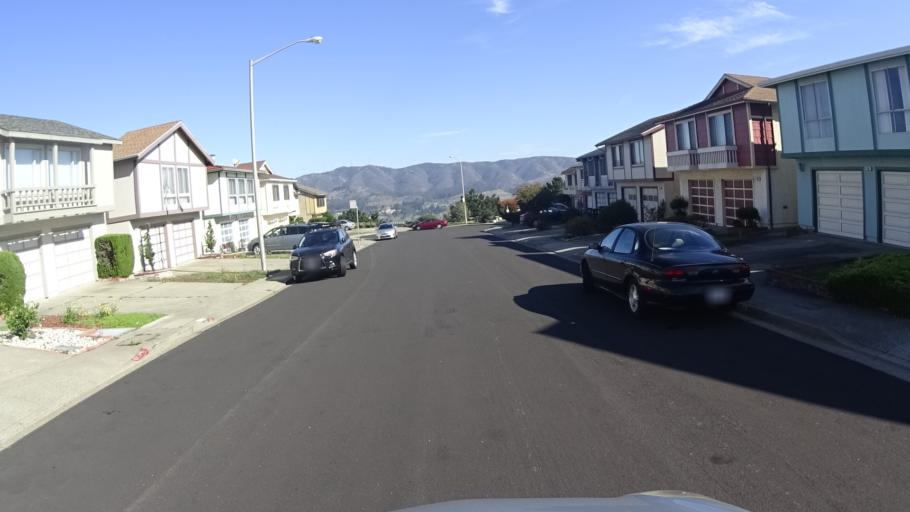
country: US
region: California
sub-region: San Mateo County
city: Colma
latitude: 37.6532
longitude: -122.4581
